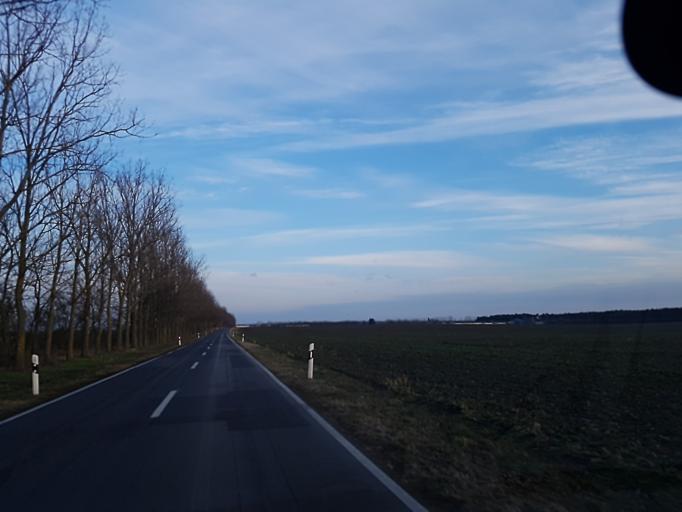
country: DE
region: Brandenburg
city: Juterbog
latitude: 51.9251
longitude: 13.0593
